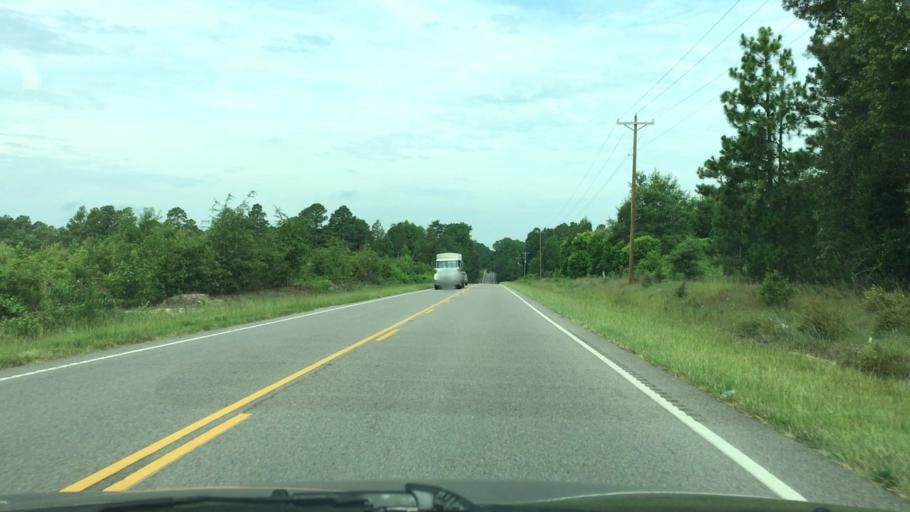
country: US
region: South Carolina
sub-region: Lexington County
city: Leesville
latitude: 33.6746
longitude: -81.4254
